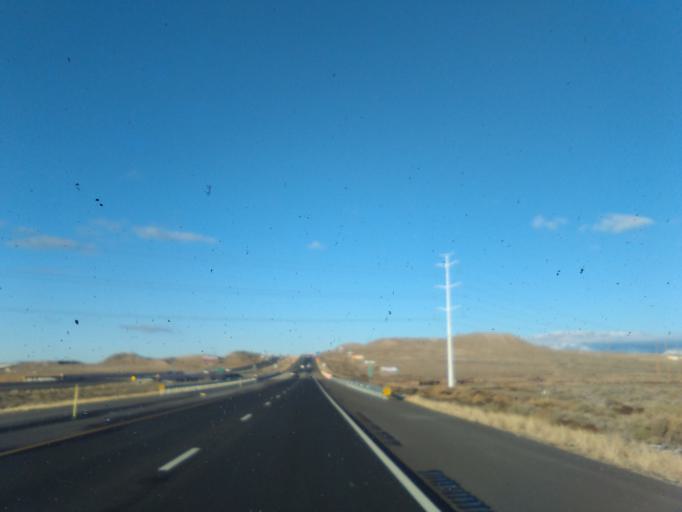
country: US
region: New Mexico
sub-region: Bernalillo County
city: South Valley
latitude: 35.0021
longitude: -106.6445
